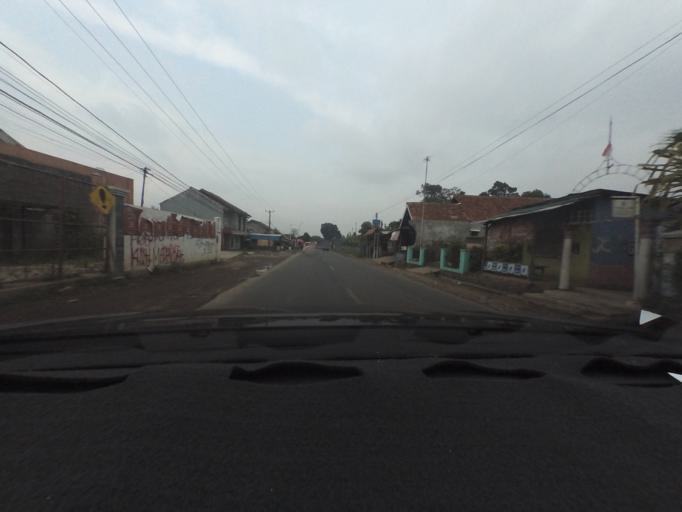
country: ID
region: West Java
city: Cicurug
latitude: -6.8185
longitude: 106.7654
